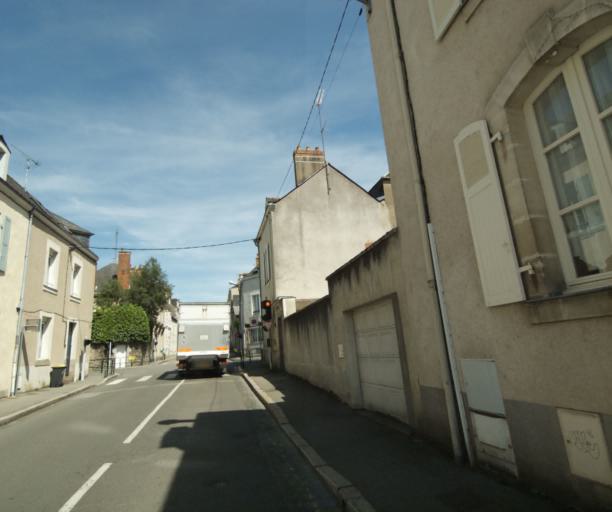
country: FR
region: Pays de la Loire
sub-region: Departement de la Mayenne
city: Laval
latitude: 48.0753
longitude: -0.7657
